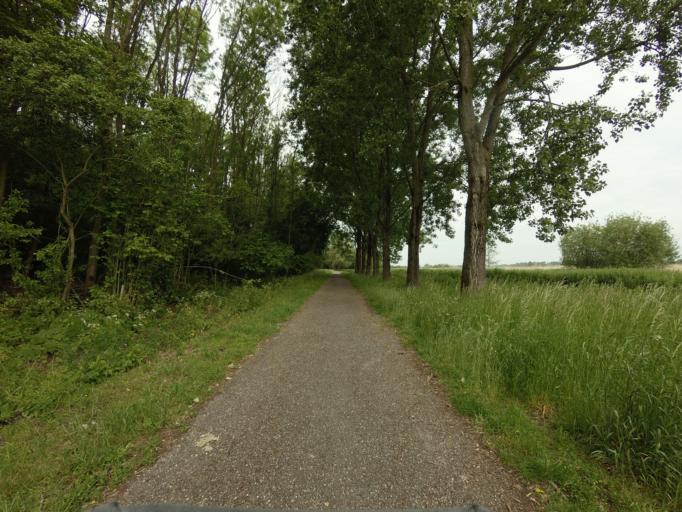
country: NL
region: North Holland
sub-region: Gemeente Medemblik
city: Medemblik
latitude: 52.7389
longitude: 5.1309
